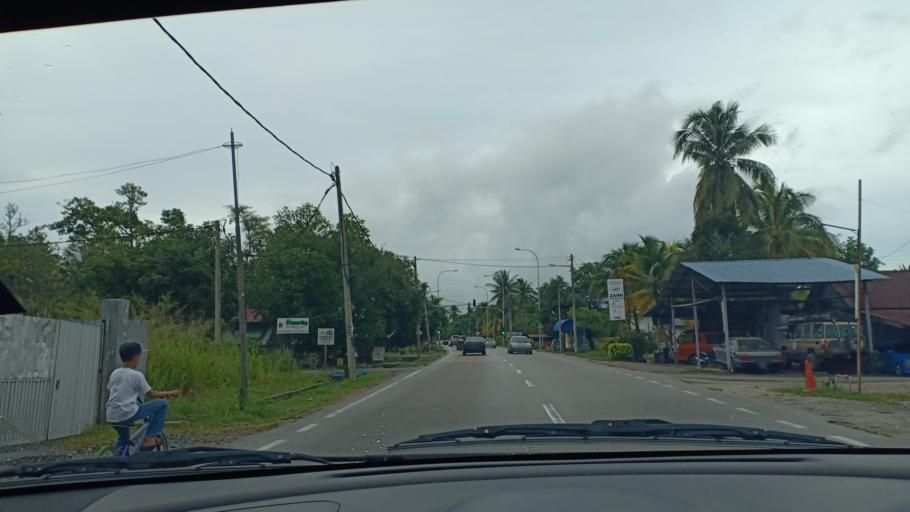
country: MY
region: Penang
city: Kepala Batas
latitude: 5.4969
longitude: 100.4440
